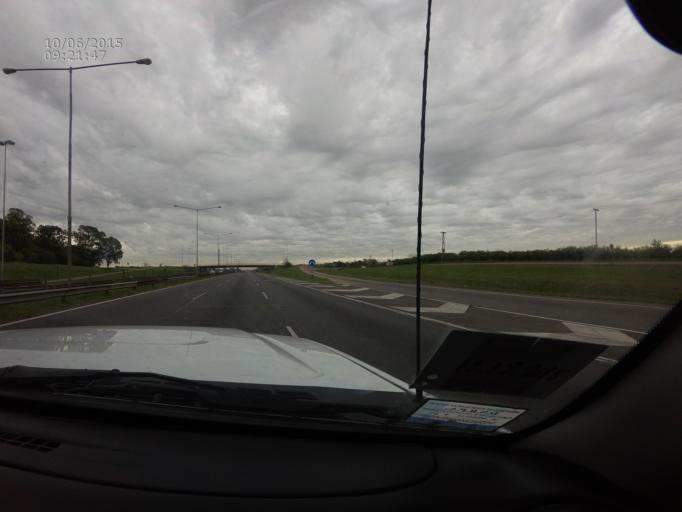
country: AR
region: Buenos Aires
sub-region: Partido de Campana
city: Campana
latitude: -34.2294
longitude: -58.9161
